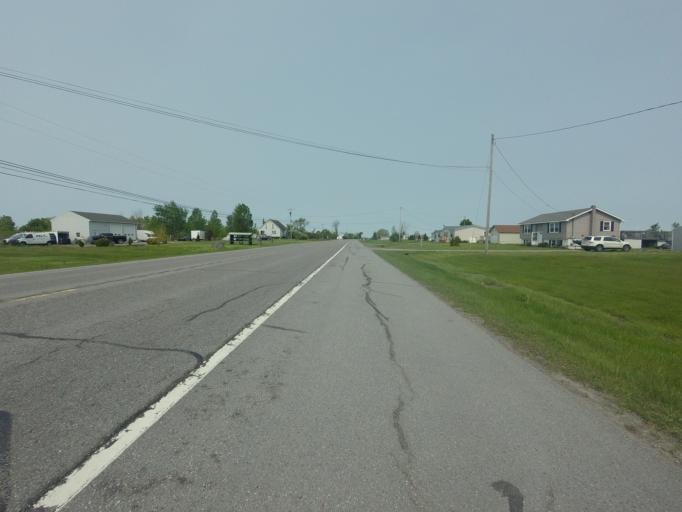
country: US
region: New York
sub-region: Jefferson County
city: Dexter
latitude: 44.0409
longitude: -76.0783
